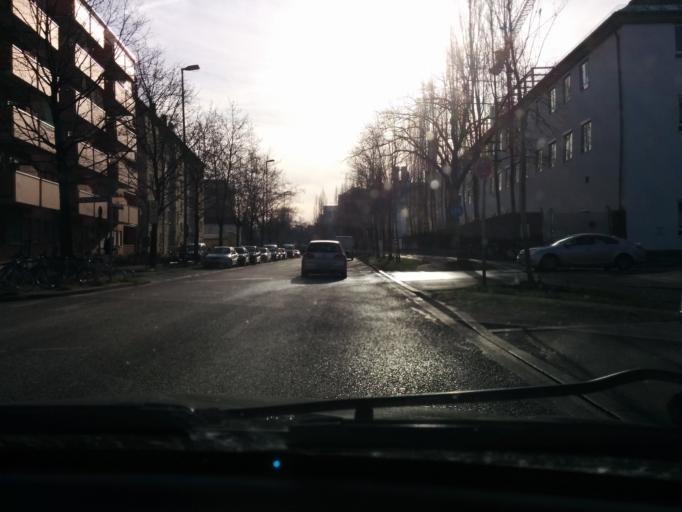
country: DE
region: Bavaria
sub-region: Upper Bavaria
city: Munich
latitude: 48.1824
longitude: 11.5632
